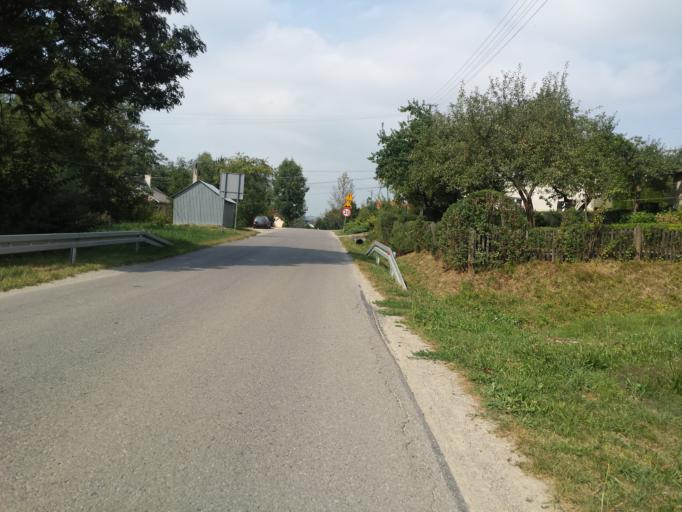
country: PL
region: Subcarpathian Voivodeship
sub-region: Powiat rzeszowski
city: Blazowa
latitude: 49.8567
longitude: 22.1317
